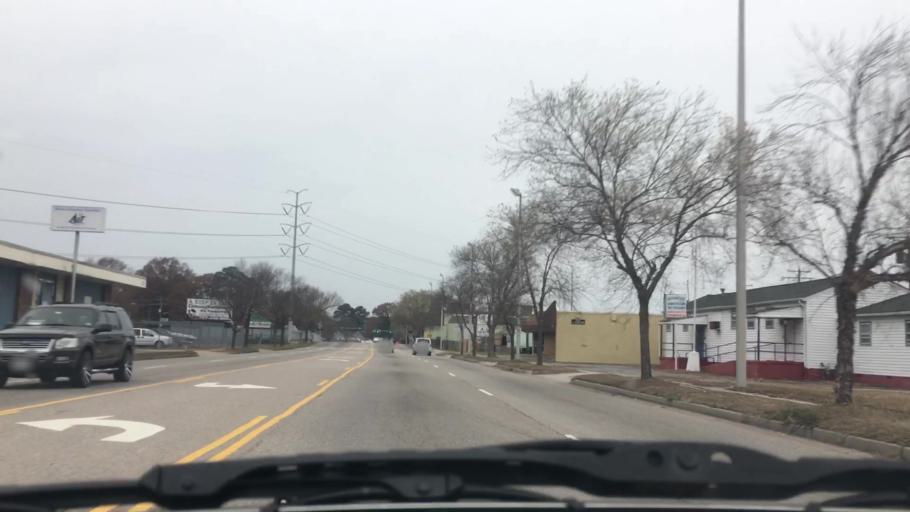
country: US
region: Virginia
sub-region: City of Norfolk
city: Norfolk
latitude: 36.8659
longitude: -76.2473
